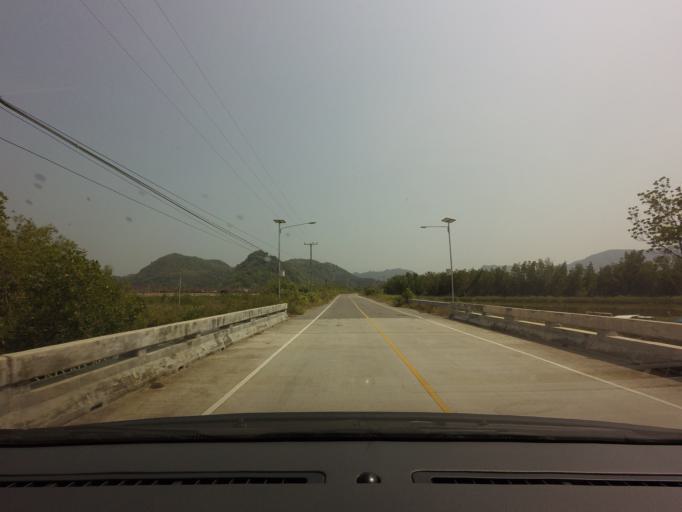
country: TH
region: Prachuap Khiri Khan
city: Sam Roi Yot
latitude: 12.1947
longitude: 99.9884
